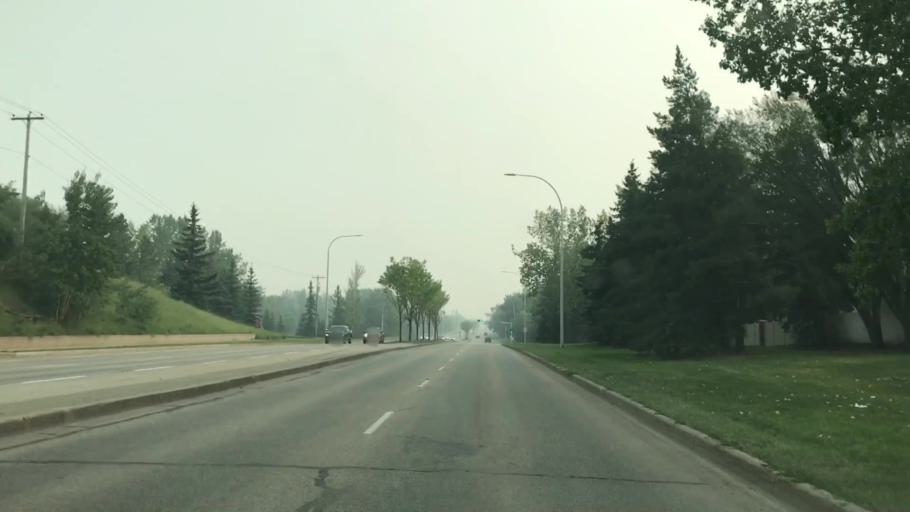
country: CA
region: Alberta
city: Sherwood Park
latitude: 53.5313
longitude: -113.3202
